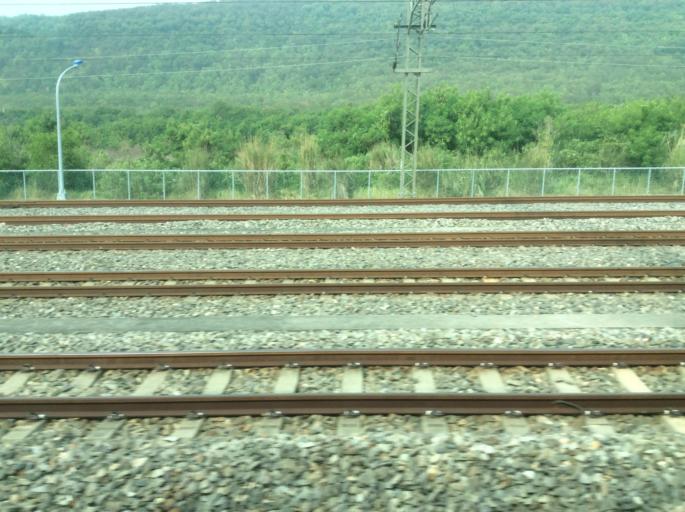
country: TW
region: Kaohsiung
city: Kaohsiung
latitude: 22.6929
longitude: 120.3132
